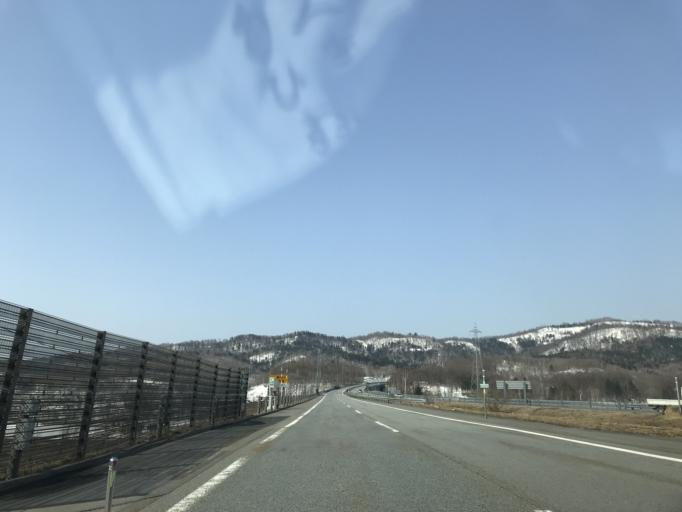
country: JP
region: Hokkaido
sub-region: Asahikawa-shi
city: Asahikawa
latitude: 43.7948
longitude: 142.2857
